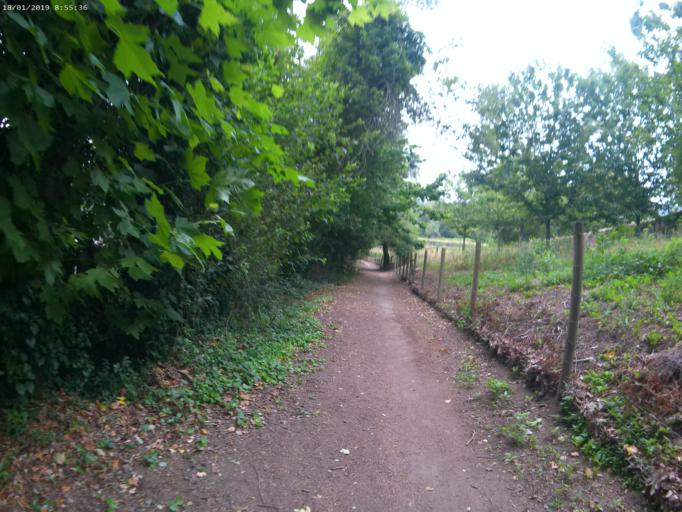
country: PT
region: Viana do Castelo
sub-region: Ponte da Barca
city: Ponte da Barca
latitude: 41.8067
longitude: -8.4358
